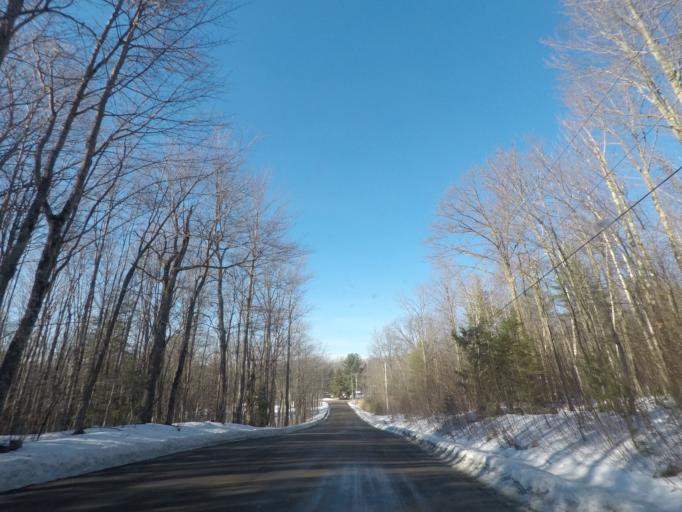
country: US
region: New York
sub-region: Rensselaer County
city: Averill Park
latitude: 42.6491
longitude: -73.5023
